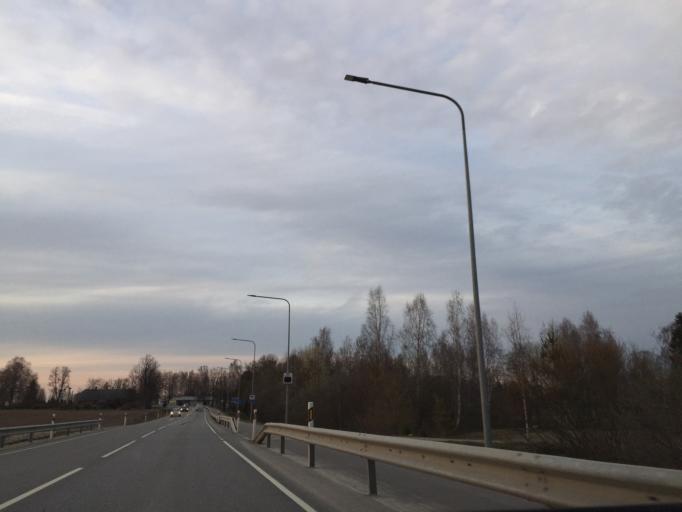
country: EE
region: Tartu
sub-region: UElenurme vald
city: Ulenurme
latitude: 58.2327
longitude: 26.6945
